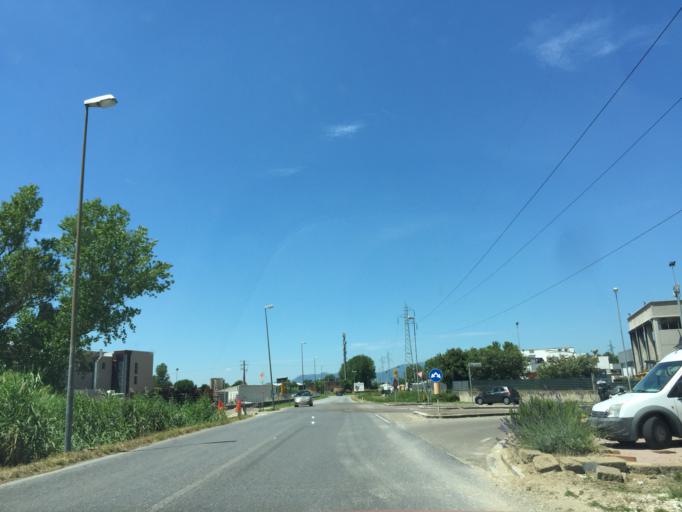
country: IT
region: Tuscany
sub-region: Province of Pisa
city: San Miniato
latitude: 43.6904
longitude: 10.7942
